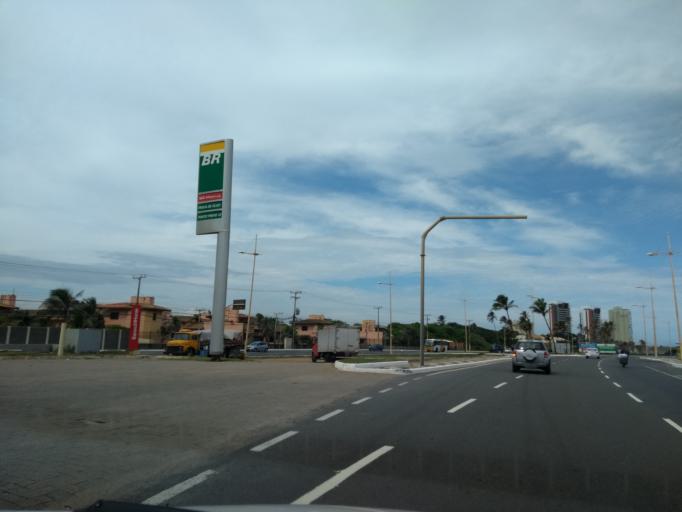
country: BR
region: Bahia
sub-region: Lauro De Freitas
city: Lauro de Freitas
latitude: -12.9632
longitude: -38.4011
